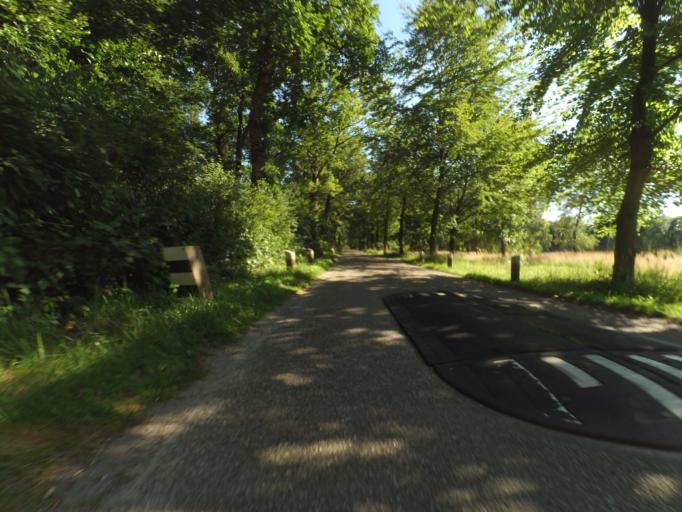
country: NL
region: Utrecht
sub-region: Gemeente Utrechtse Heuvelrug
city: Maarsbergen
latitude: 52.0623
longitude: 5.3973
